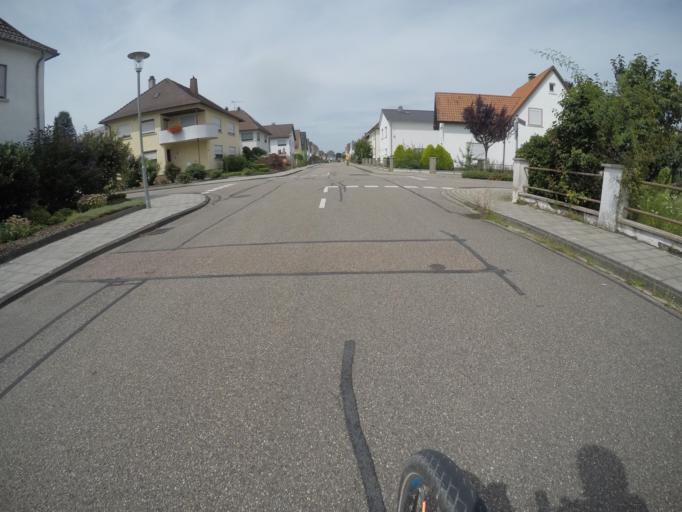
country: DE
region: Baden-Wuerttemberg
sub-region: Karlsruhe Region
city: Forst
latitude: 49.1471
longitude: 8.5859
